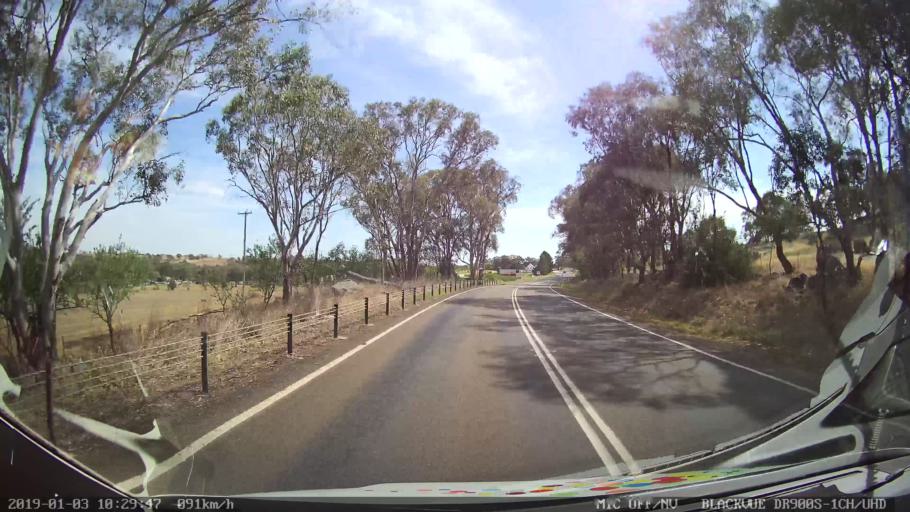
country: AU
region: New South Wales
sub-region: Young
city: Young
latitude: -34.3695
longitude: 148.2617
